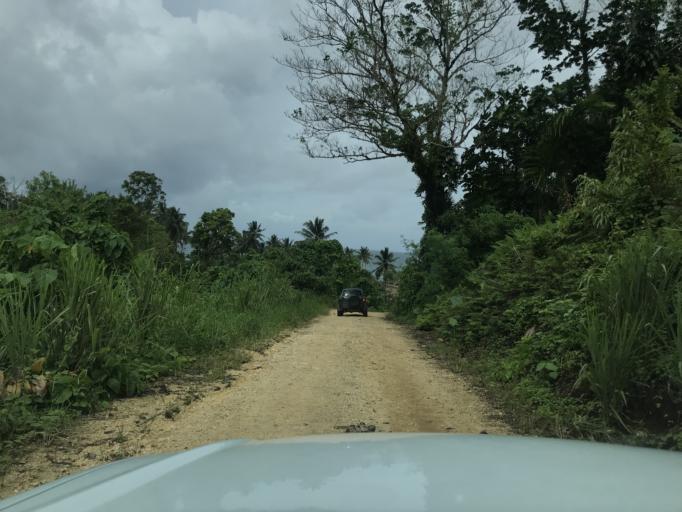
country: SB
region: Malaita
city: Auki
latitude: -8.6316
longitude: 160.6618
